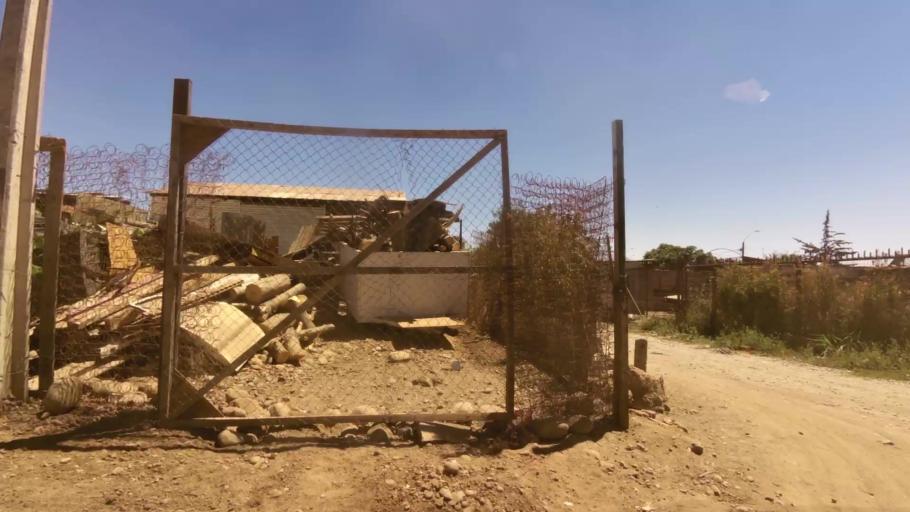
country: CL
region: O'Higgins
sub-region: Provincia de Cachapoal
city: Machali
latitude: -34.1658
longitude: -70.6955
